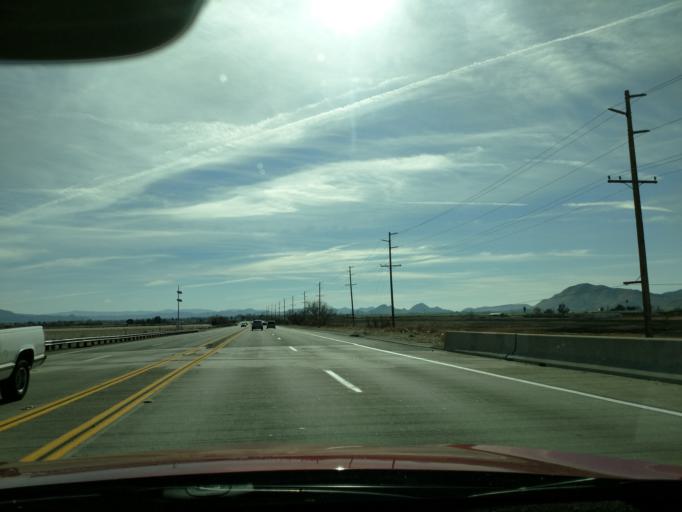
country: US
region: California
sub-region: Riverside County
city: San Jacinto
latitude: 33.8309
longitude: -117.0036
